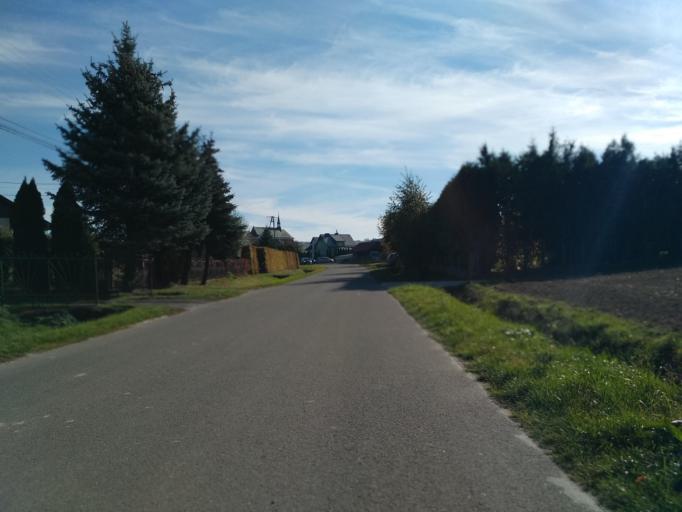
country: PL
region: Subcarpathian Voivodeship
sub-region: Powiat ropczycko-sedziszowski
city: Iwierzyce
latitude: 50.0619
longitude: 21.7829
